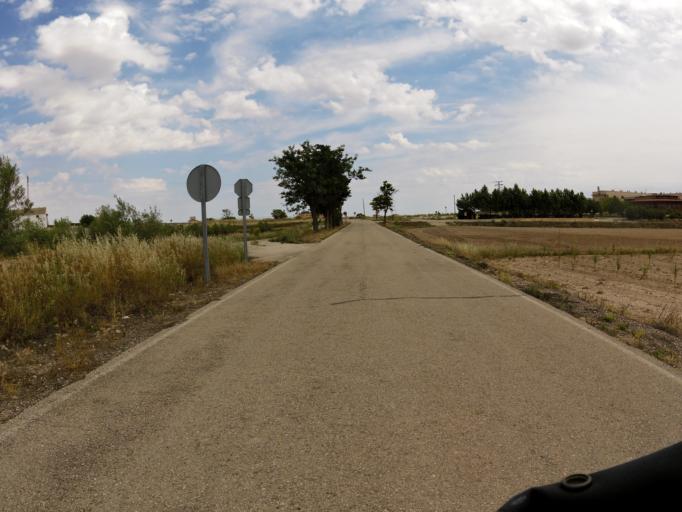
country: ES
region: Castille-La Mancha
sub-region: Provincia de Albacete
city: Valdeganga
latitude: 39.1266
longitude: -1.6811
